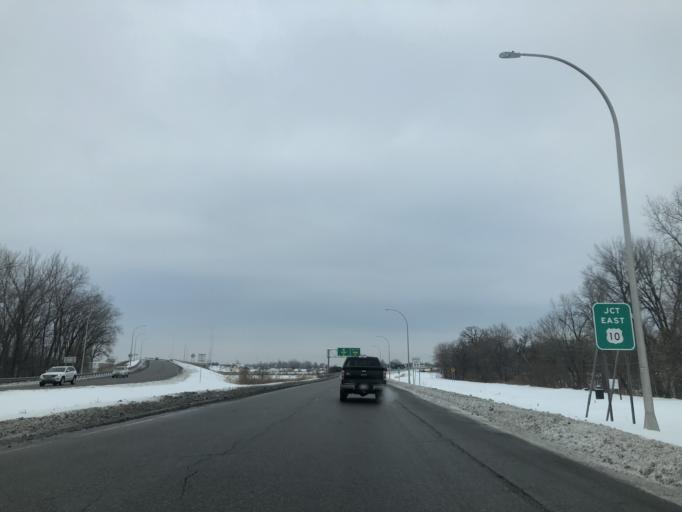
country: US
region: Minnesota
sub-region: Ramsey County
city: Mounds View
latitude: 45.0941
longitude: -93.1925
